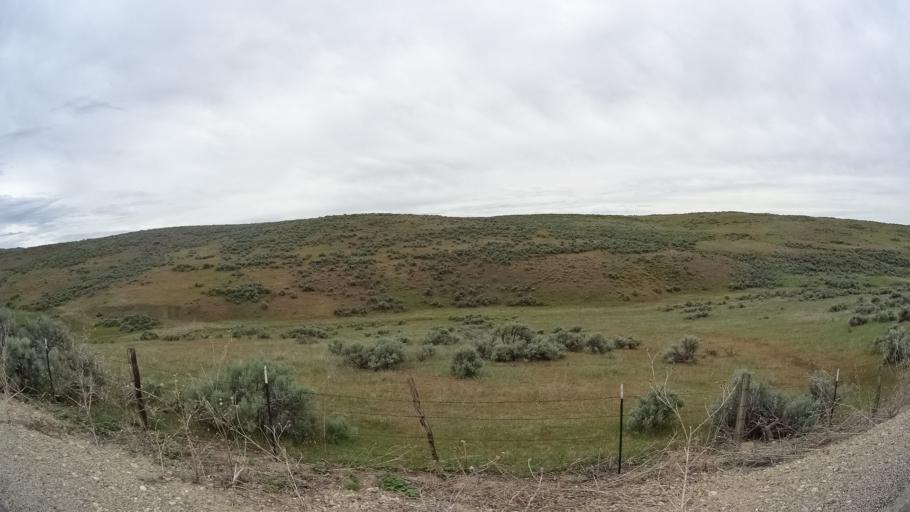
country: US
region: Idaho
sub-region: Ada County
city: Boise
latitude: 43.4824
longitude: -116.0202
